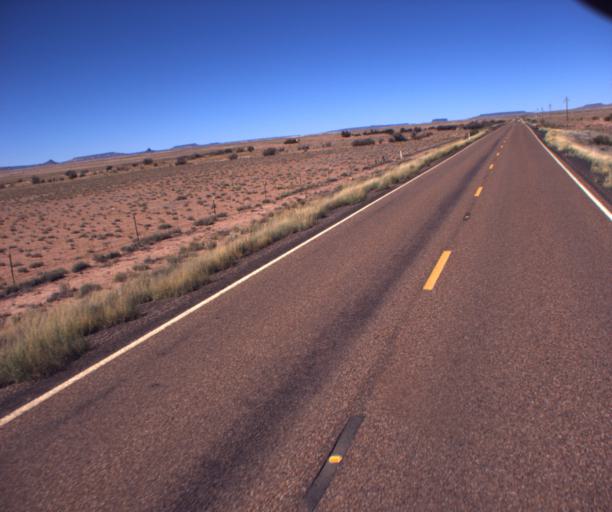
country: US
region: Arizona
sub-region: Navajo County
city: Holbrook
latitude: 35.0766
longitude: -110.0994
